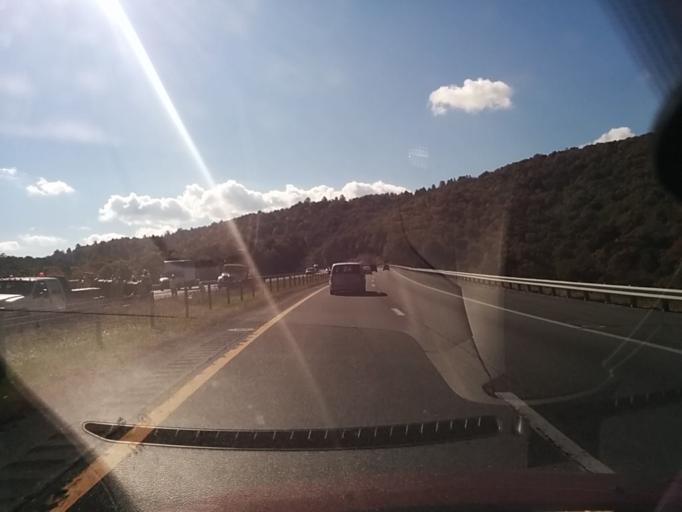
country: US
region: Virginia
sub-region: City of Waynesboro
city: Waynesboro
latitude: 38.0383
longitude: -78.8715
